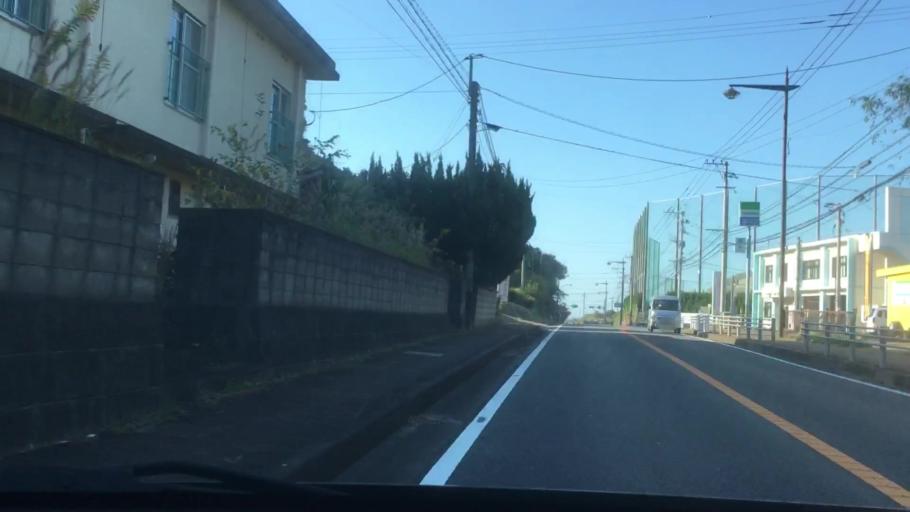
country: JP
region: Nagasaki
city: Togitsu
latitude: 32.9391
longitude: 129.6539
